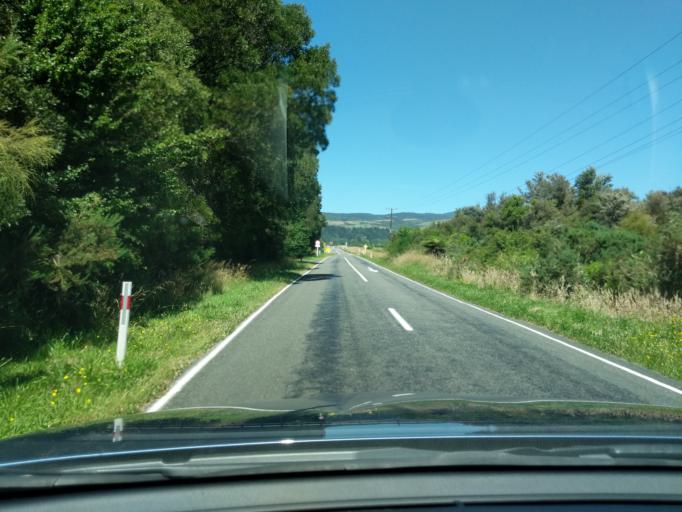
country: NZ
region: Tasman
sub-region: Tasman District
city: Takaka
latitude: -40.7274
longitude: 172.6079
